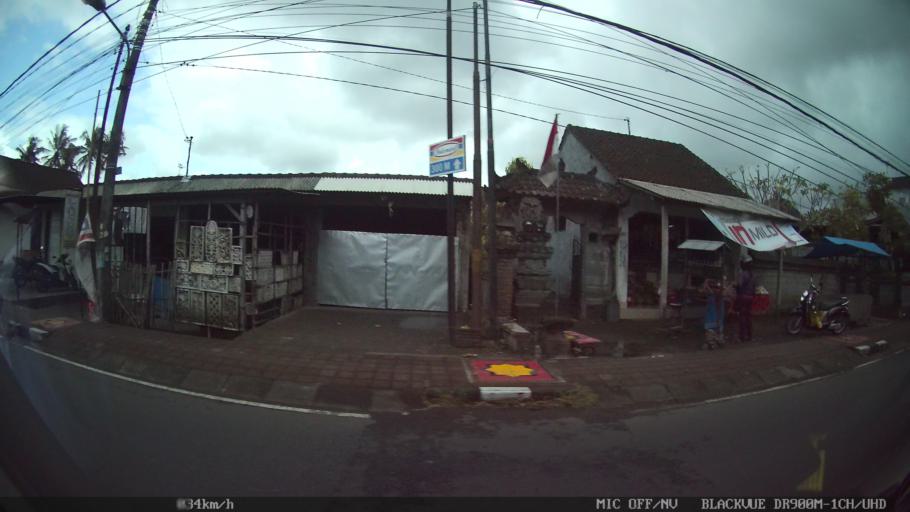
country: ID
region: Bali
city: Banjar Cemenggon
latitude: -8.5336
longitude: 115.2001
